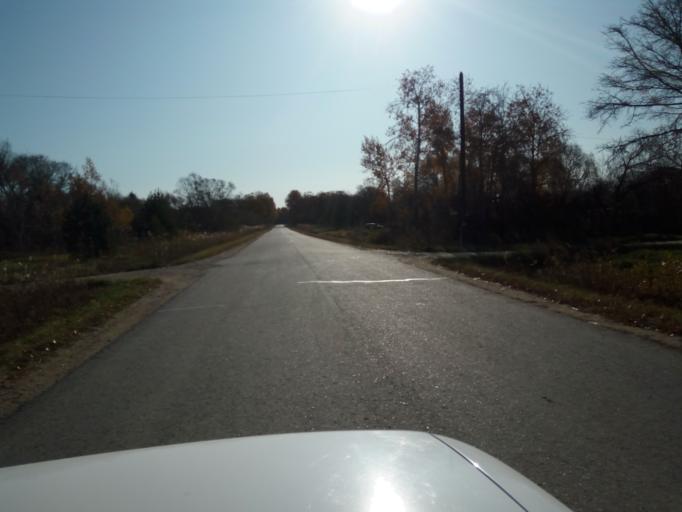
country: RU
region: Primorskiy
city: Lazo
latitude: 45.8727
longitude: 133.6548
